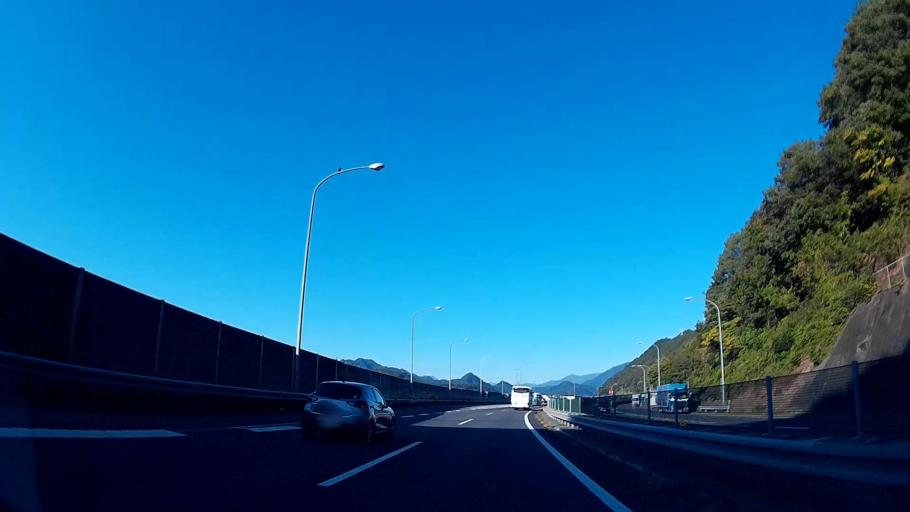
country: JP
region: Yamanashi
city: Uenohara
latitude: 35.6157
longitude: 139.1599
